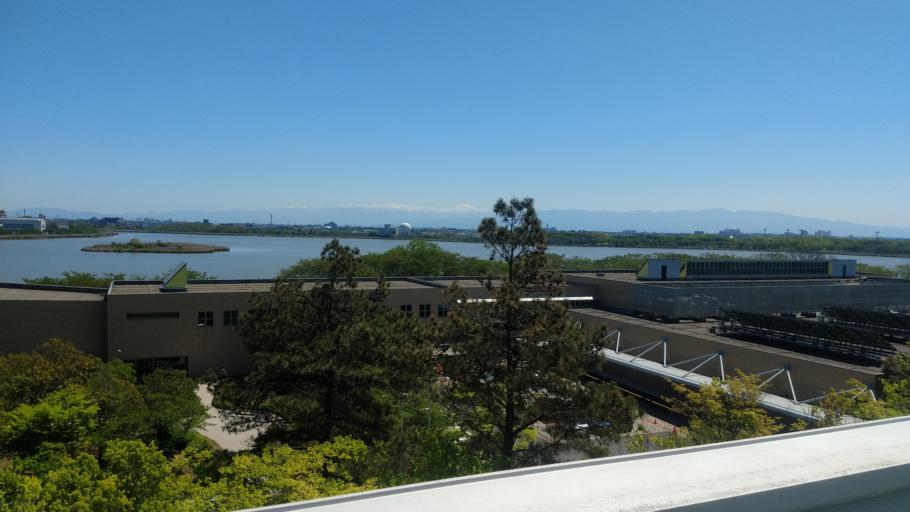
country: JP
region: Niigata
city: Niigata-shi
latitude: 37.8907
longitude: 139.0502
